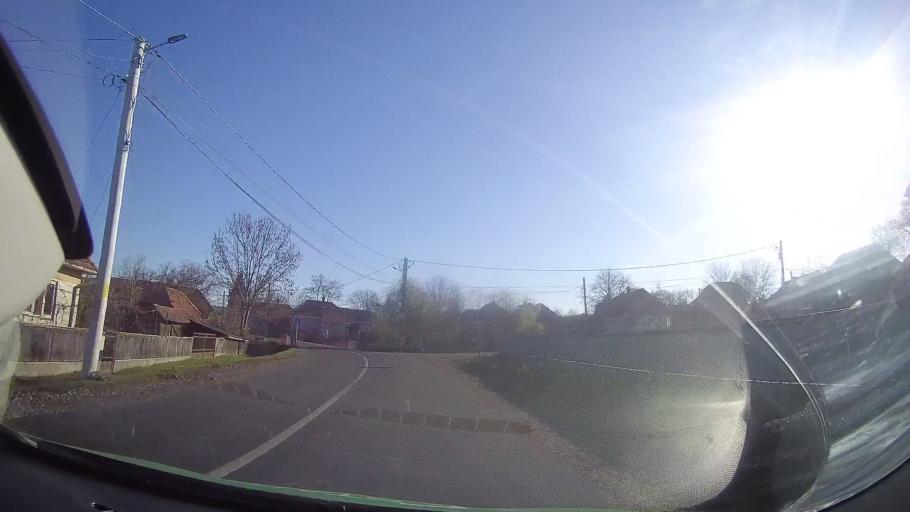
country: RO
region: Mures
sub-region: Comuna Band
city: Band
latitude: 46.5804
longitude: 24.3641
